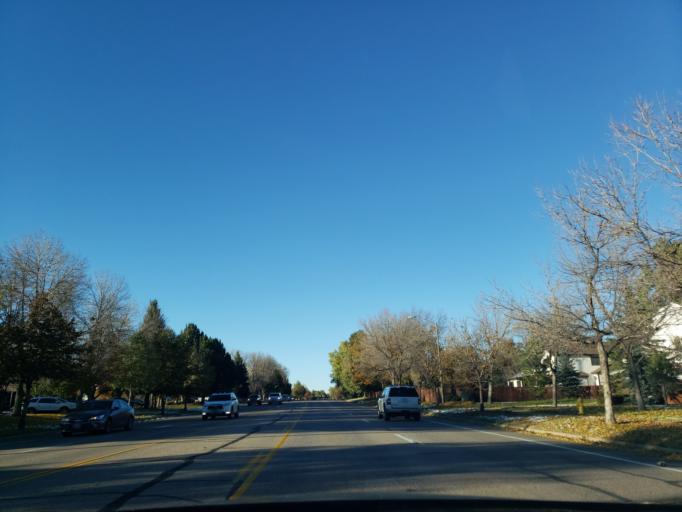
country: US
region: Colorado
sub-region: Larimer County
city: Fort Collins
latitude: 40.5162
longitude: -105.0581
